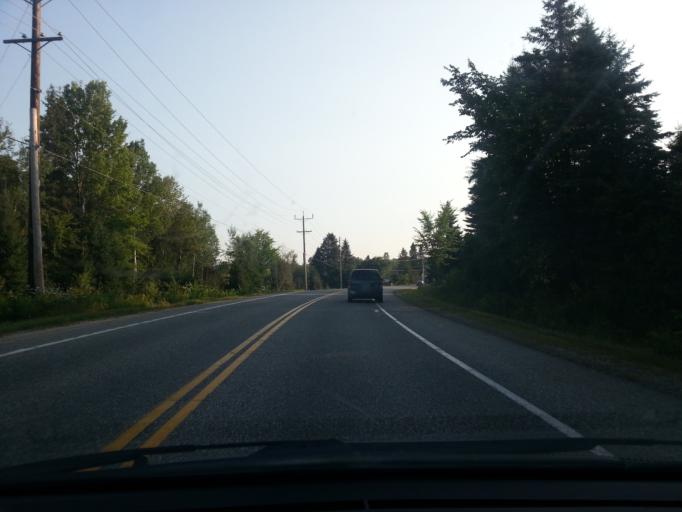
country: CA
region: Quebec
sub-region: Outaouais
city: Wakefield
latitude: 45.9263
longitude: -76.0170
